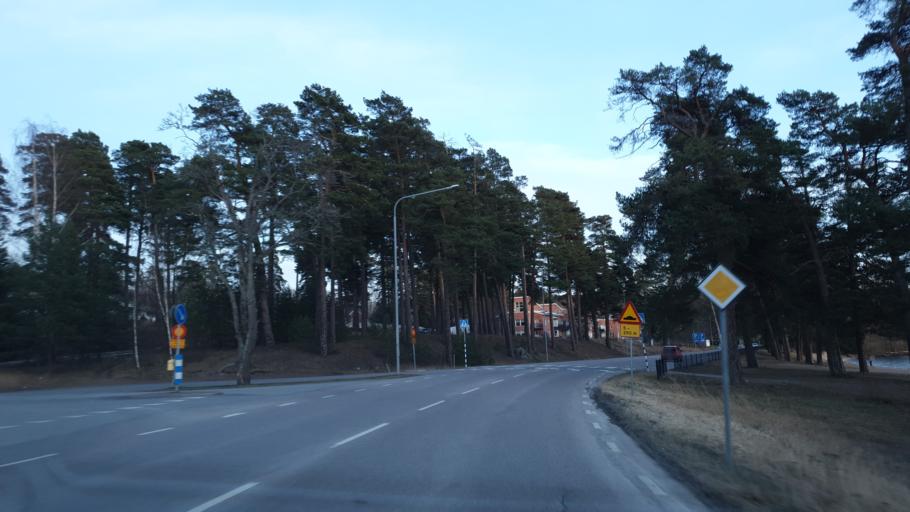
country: SE
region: Uppsala
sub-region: Habo Kommun
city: Balsta
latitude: 59.5530
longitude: 17.5532
